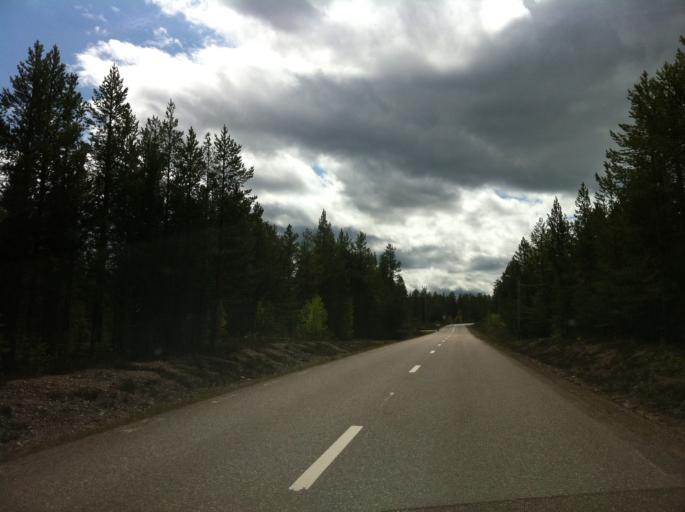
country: NO
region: Hedmark
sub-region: Trysil
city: Innbygda
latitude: 61.6841
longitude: 13.1278
